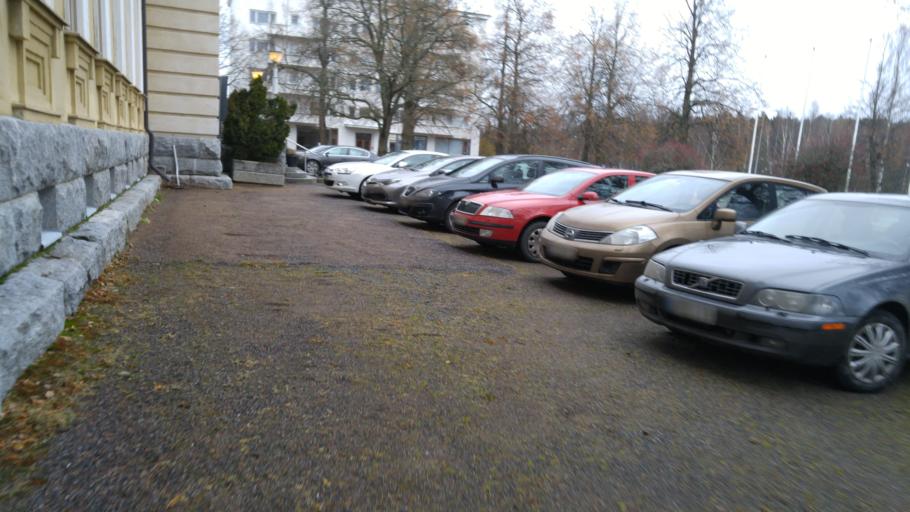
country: FI
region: Pirkanmaa
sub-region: Ylae-Pirkanmaa
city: Maenttae
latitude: 62.0275
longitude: 24.6440
